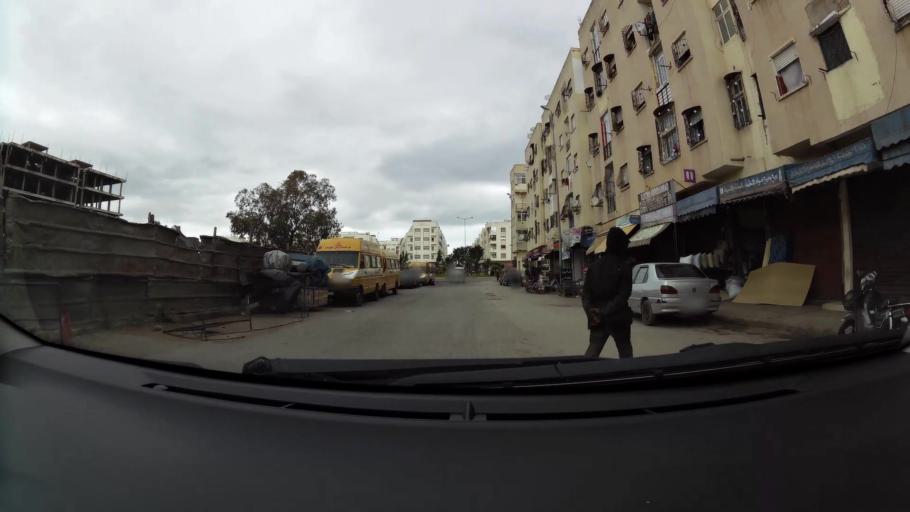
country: MA
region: Grand Casablanca
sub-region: Mediouna
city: Tit Mellil
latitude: 33.5575
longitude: -7.5326
